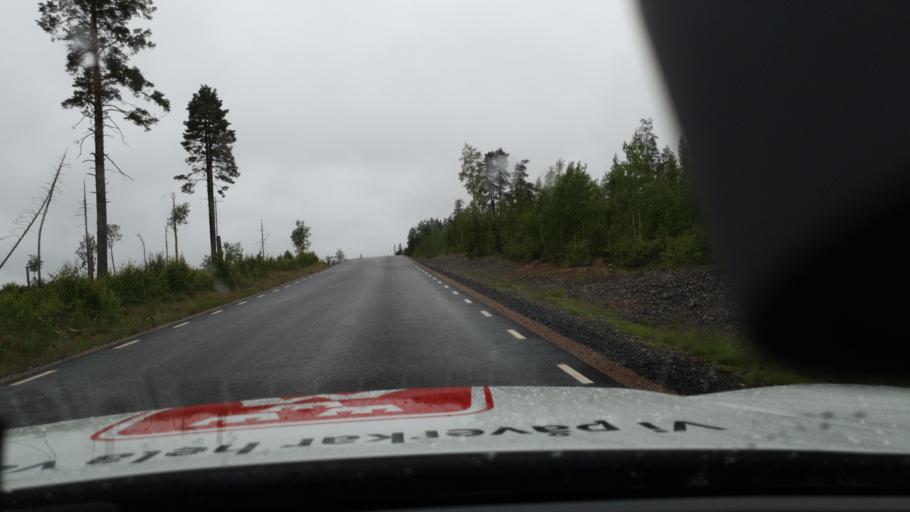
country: SE
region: Norrbotten
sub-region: Overtornea Kommun
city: OEvertornea
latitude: 66.5798
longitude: 23.3298
